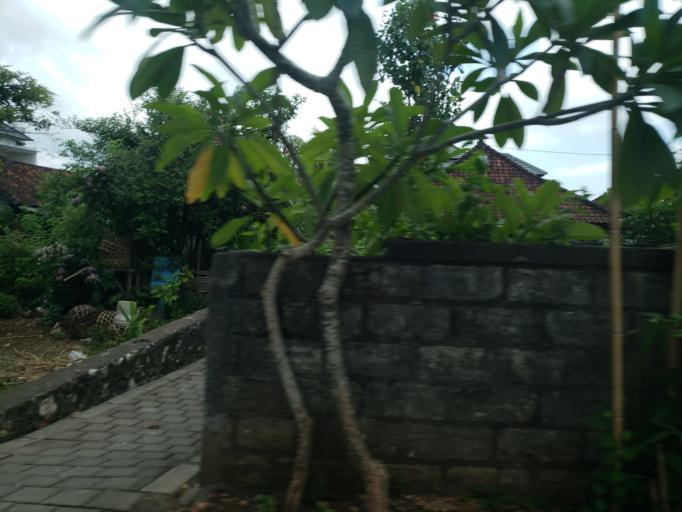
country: ID
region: Bali
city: Kangin
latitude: -8.8326
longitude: 115.1496
